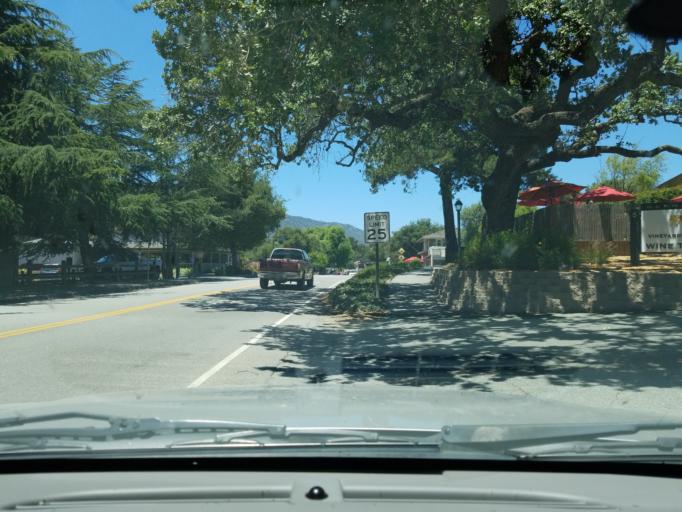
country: US
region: California
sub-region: Monterey County
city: Carmel Valley Village
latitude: 36.4788
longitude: -121.7305
